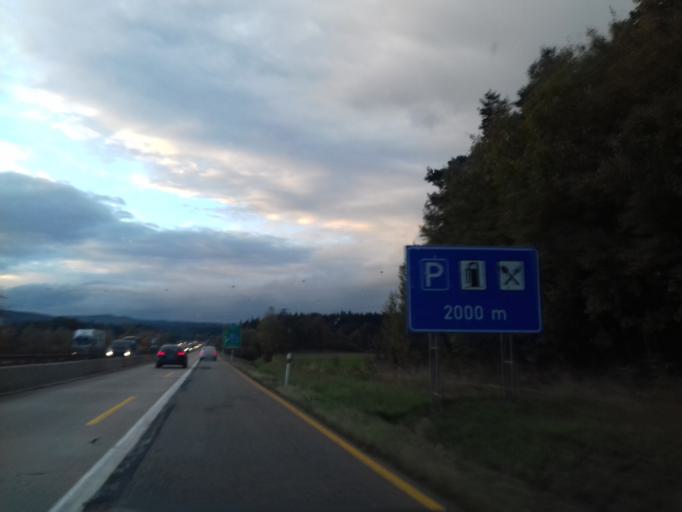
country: CZ
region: Vysocina
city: Dobronin
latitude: 49.4460
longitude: 15.6236
